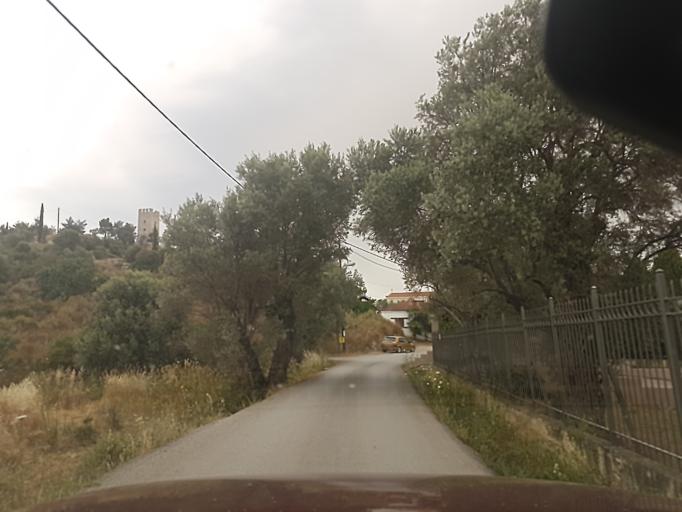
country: GR
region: Central Greece
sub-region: Nomos Evvoias
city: Mytikas
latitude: 38.4448
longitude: 23.6675
